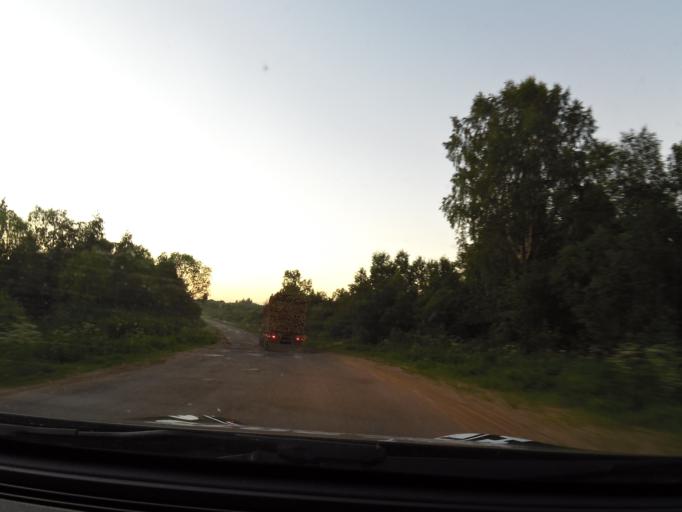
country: RU
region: Vologda
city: Vytegra
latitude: 60.8749
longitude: 36.0334
